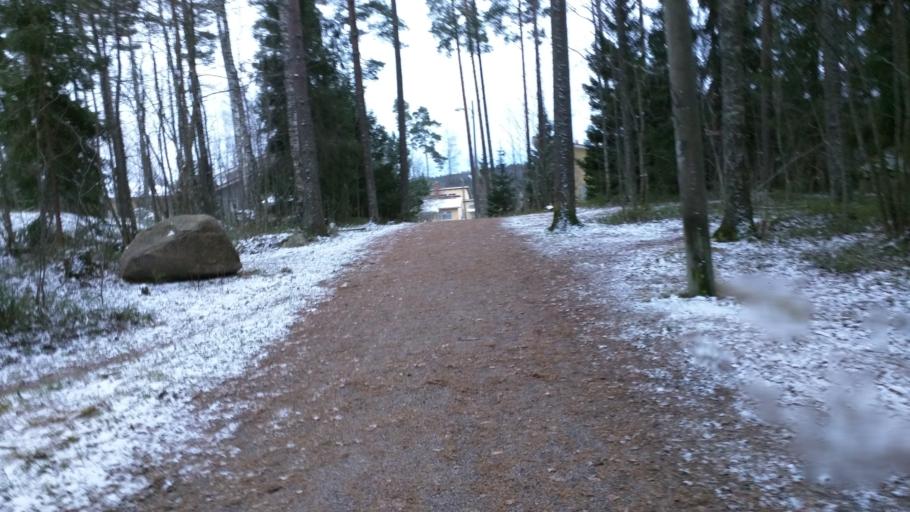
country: FI
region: Uusimaa
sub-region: Helsinki
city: Kilo
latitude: 60.2435
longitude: 24.7708
